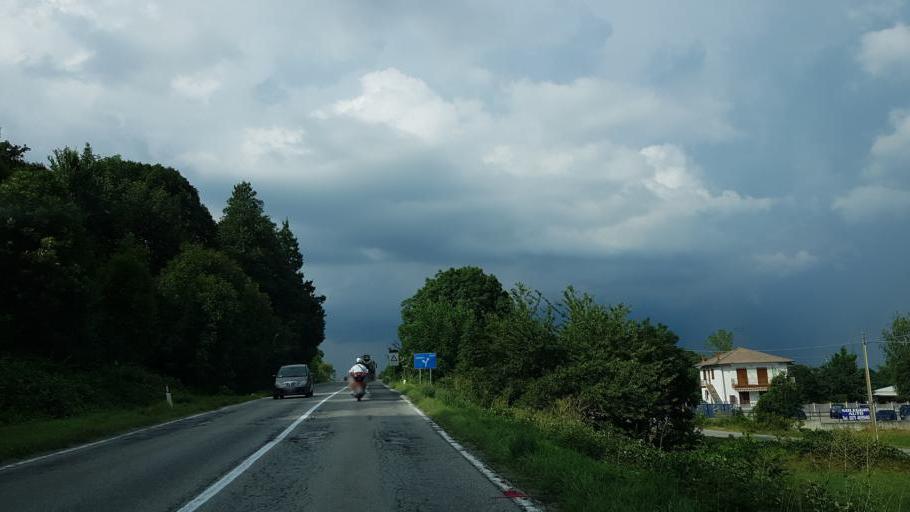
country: IT
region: Piedmont
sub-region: Provincia di Cuneo
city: Vignolo
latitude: 44.3526
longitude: 7.4776
